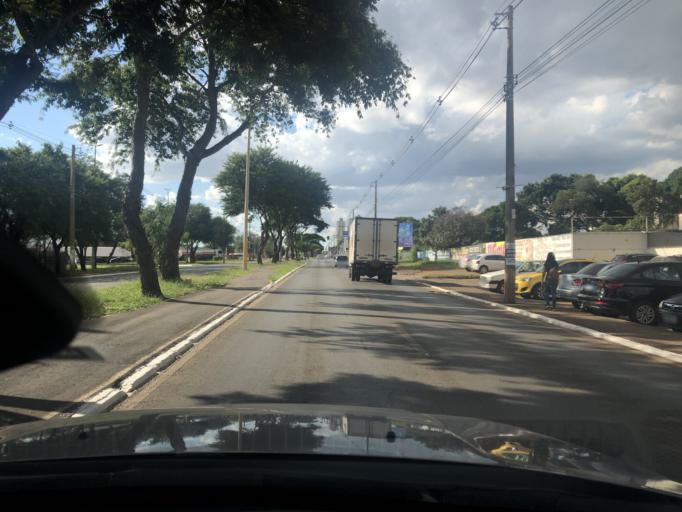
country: BR
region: Federal District
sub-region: Brasilia
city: Brasilia
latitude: -16.0102
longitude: -48.0598
